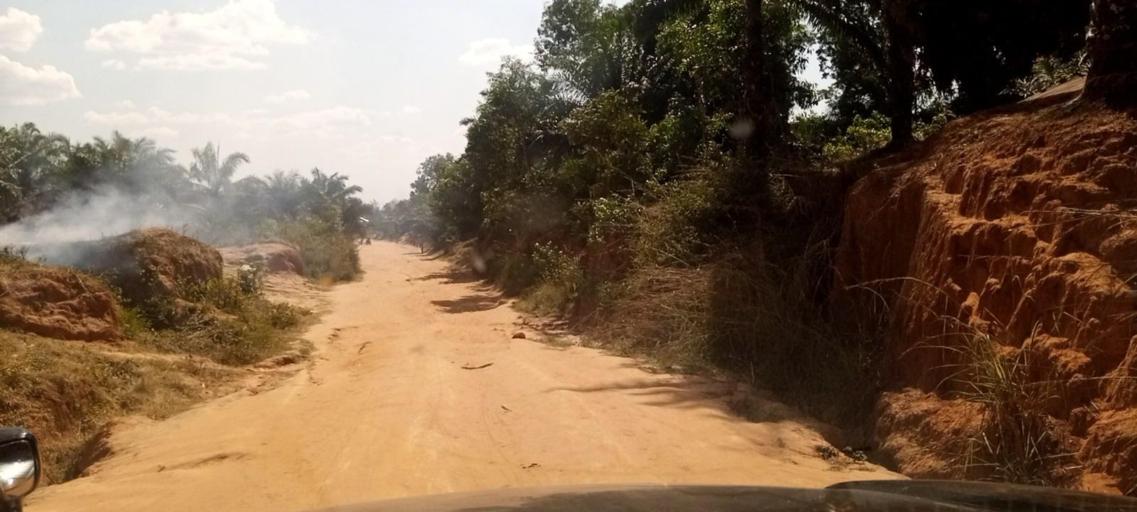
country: CD
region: Kasai-Oriental
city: Kabinda
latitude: -6.1295
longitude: 24.5219
